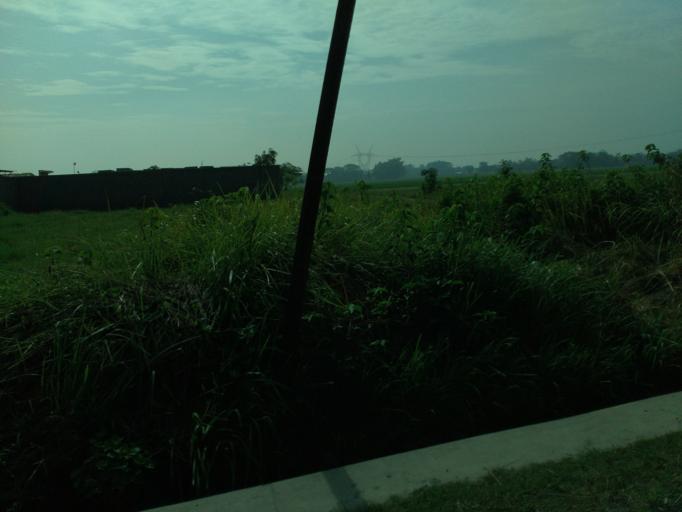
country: ID
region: Central Java
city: Delanggu
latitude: -7.6430
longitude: 110.6891
